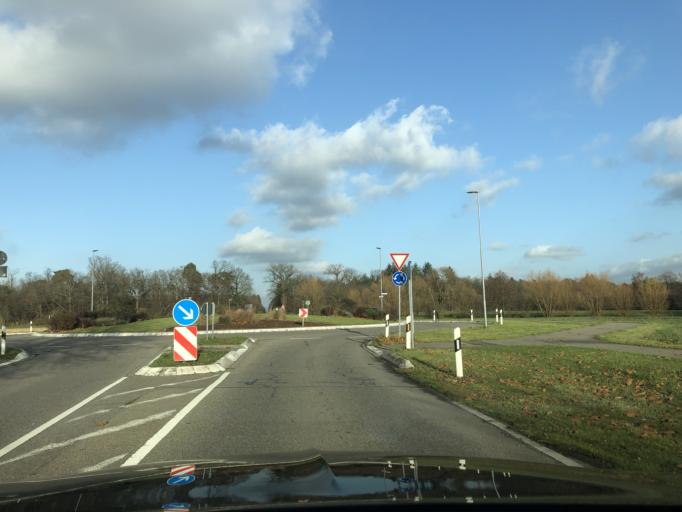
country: DE
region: Baden-Wuerttemberg
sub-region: Karlsruhe Region
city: Waghausel
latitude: 49.2526
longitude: 8.5460
